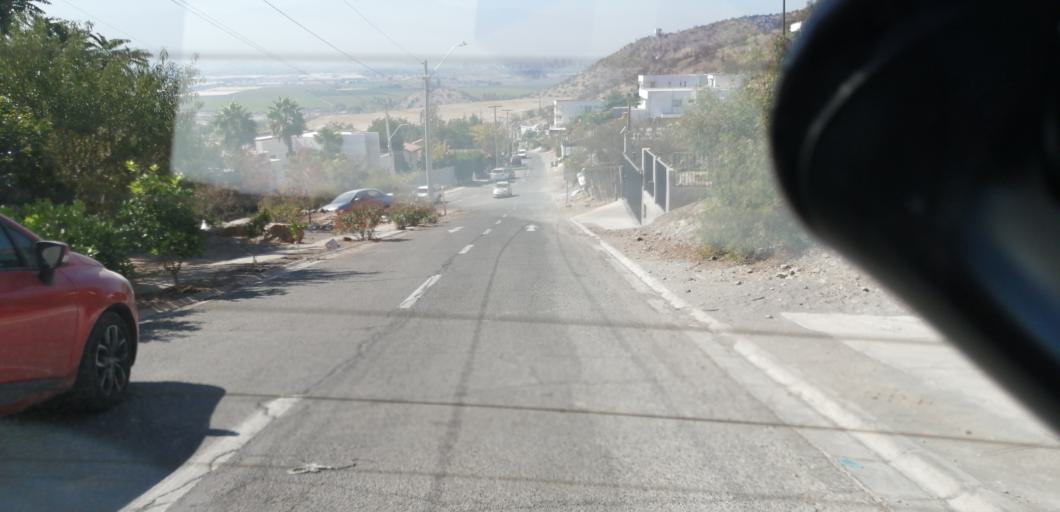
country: CL
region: Santiago Metropolitan
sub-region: Provincia de Santiago
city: Lo Prado
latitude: -33.4593
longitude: -70.8223
